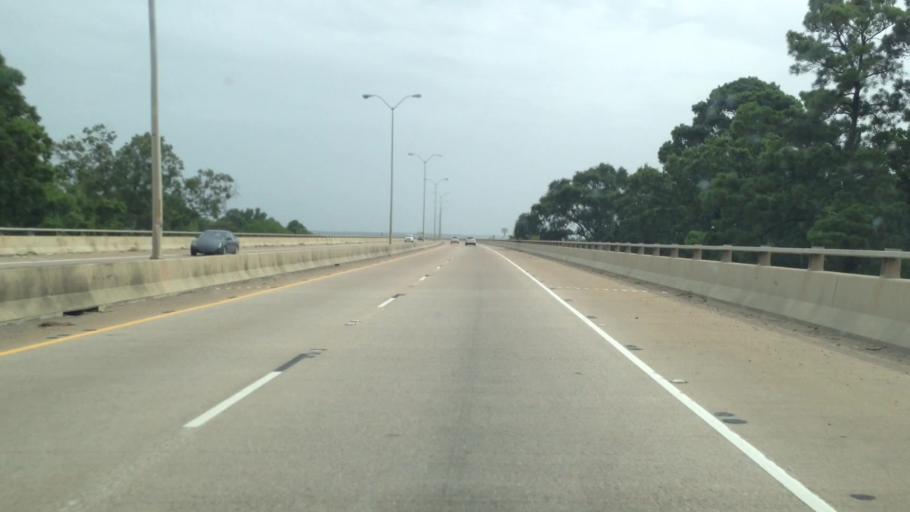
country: US
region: Louisiana
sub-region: Caddo Parish
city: Shreveport
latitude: 32.4950
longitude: -93.8215
